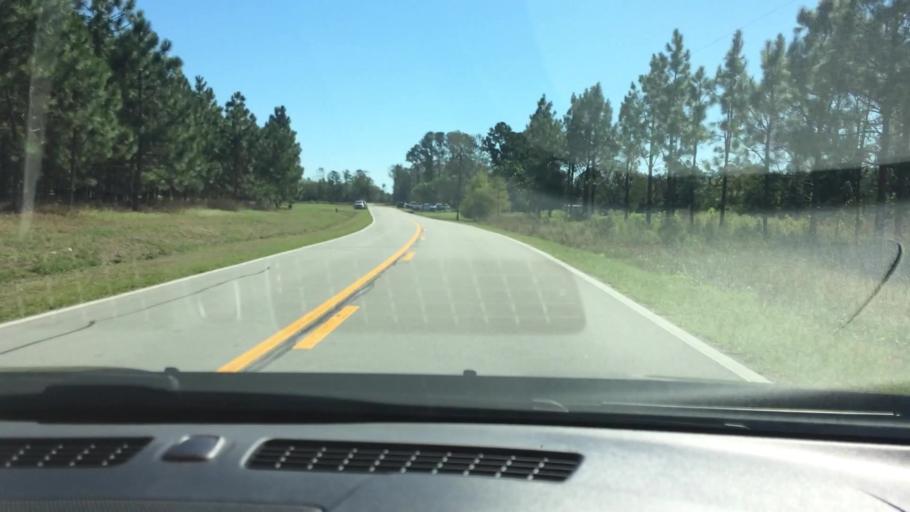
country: US
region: North Carolina
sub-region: Craven County
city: Vanceboro
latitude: 35.3244
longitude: -77.2964
